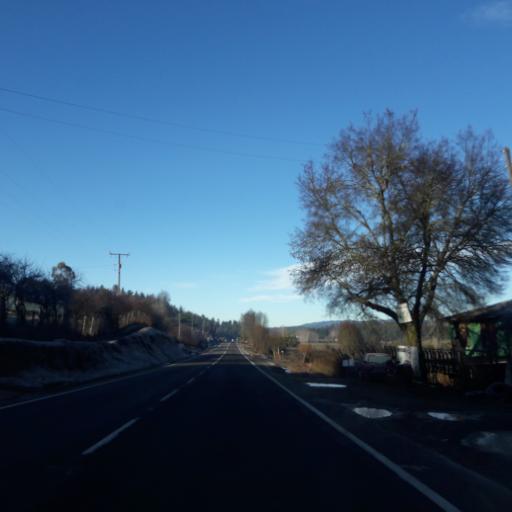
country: CL
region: Biobio
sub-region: Provincia de Biobio
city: La Laja
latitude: -37.3059
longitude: -72.9261
